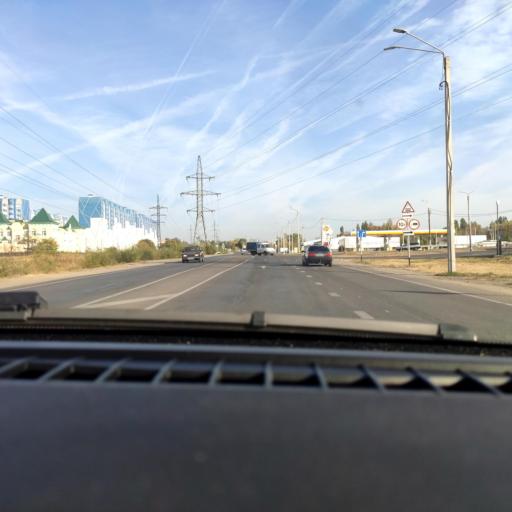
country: RU
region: Voronezj
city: Maslovka
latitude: 51.5900
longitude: 39.2483
